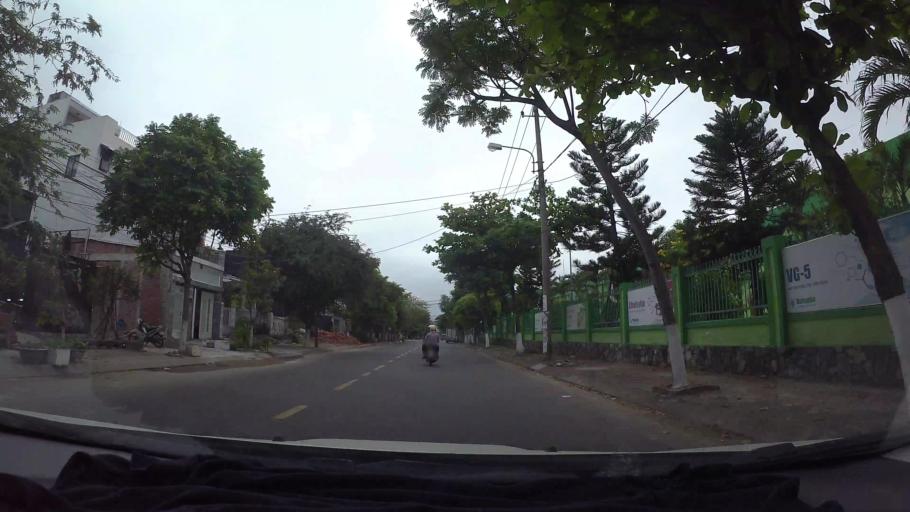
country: VN
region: Da Nang
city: Lien Chieu
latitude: 16.0774
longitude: 108.1695
